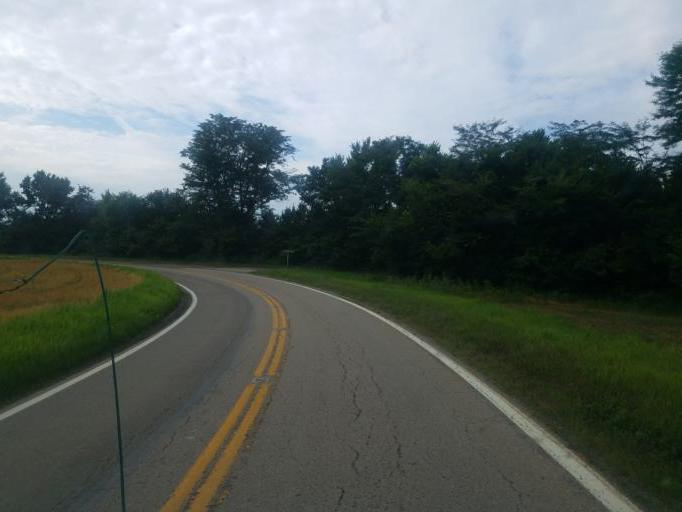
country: US
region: Ohio
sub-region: Knox County
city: Oak Hill
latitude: 40.3537
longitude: -82.0945
